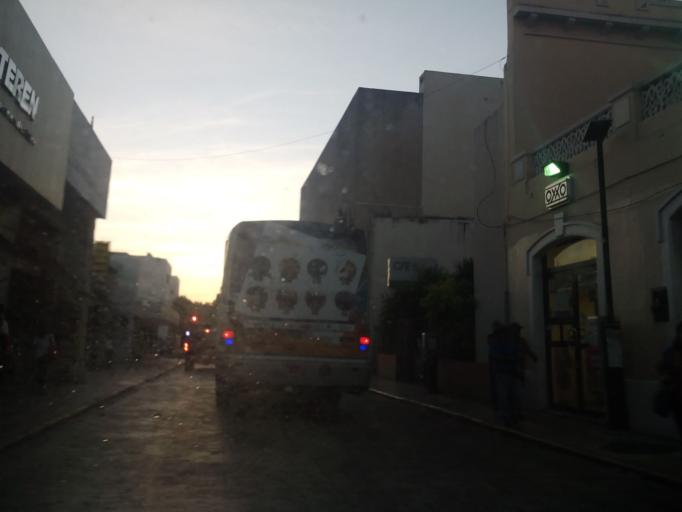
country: MX
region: Yucatan
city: Merida
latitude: 20.9684
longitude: -89.6210
